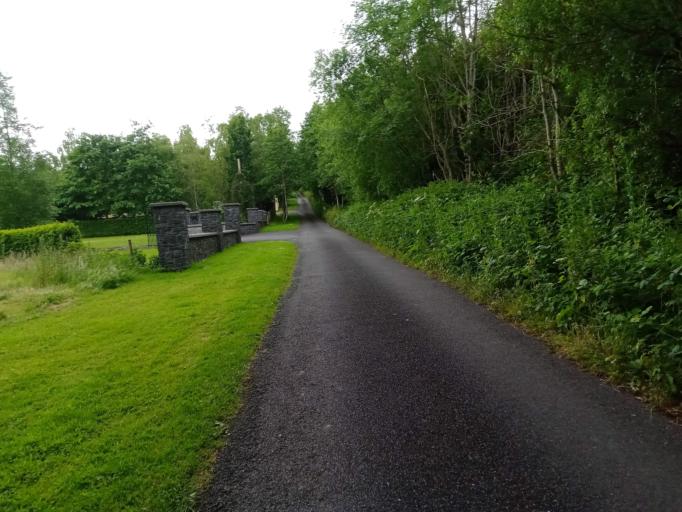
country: IE
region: Leinster
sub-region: Kilkenny
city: Piltown
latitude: 52.4544
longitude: -7.2772
